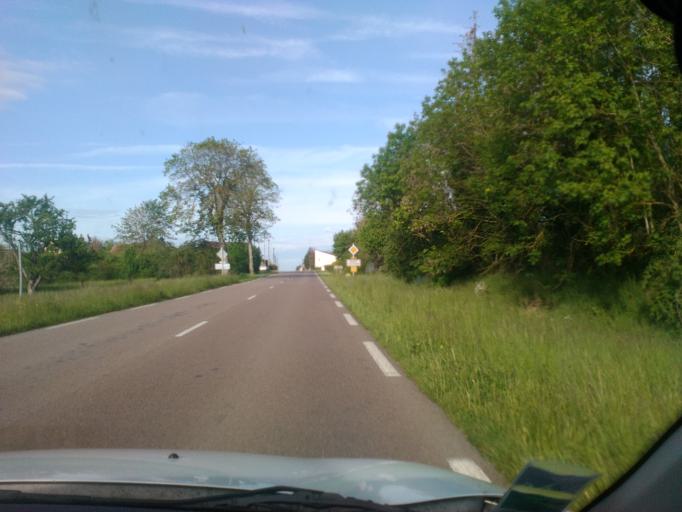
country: FR
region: Champagne-Ardenne
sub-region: Departement de l'Aube
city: Vendeuvre-sur-Barse
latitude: 48.2441
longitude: 4.5426
